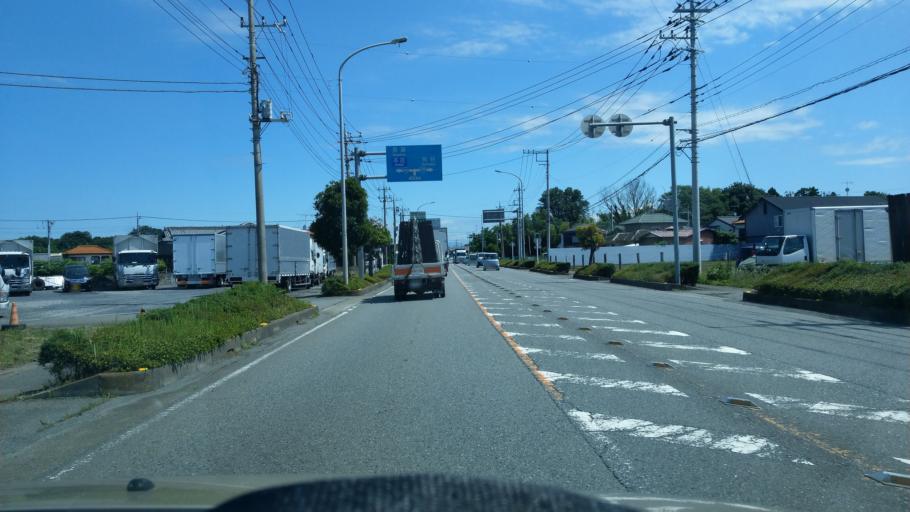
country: JP
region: Saitama
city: Yorii
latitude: 36.1177
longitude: 139.2109
